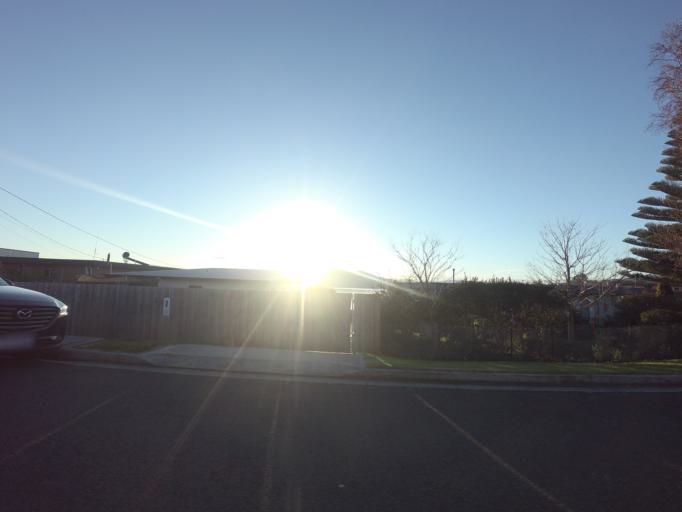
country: AU
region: Tasmania
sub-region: Sorell
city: Sorell
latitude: -42.8017
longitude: 147.5267
